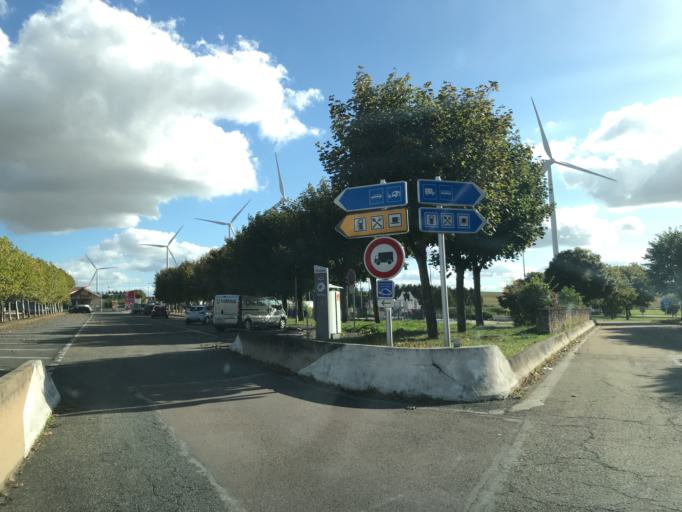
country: FR
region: Bourgogne
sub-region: Departement de l'Yonne
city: Venoy
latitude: 47.7899
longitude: 3.6693
